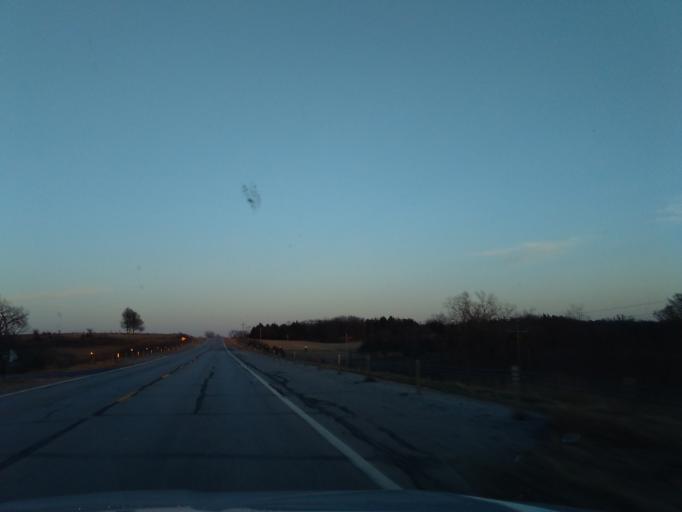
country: US
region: Nebraska
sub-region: Pawnee County
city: Pawnee City
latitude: 40.1781
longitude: -96.0441
